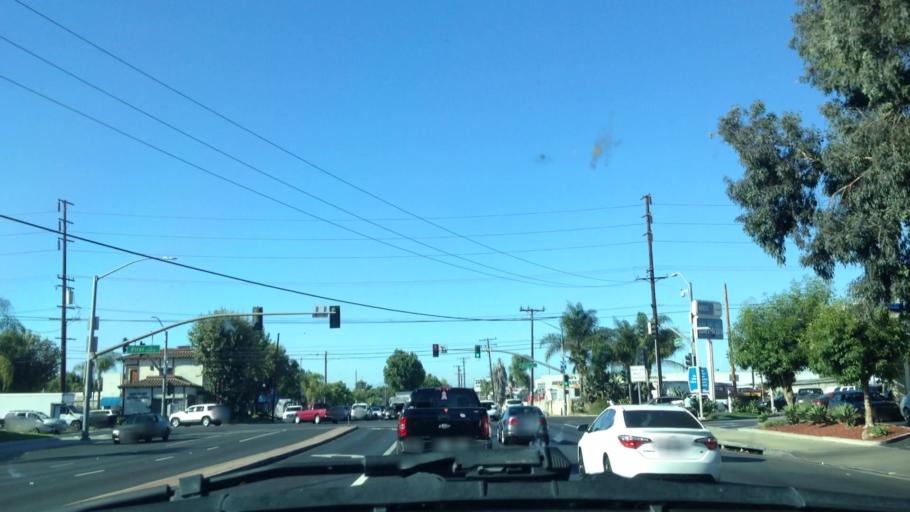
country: US
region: California
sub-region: Orange County
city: Santa Ana
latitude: 33.7445
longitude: -117.9053
